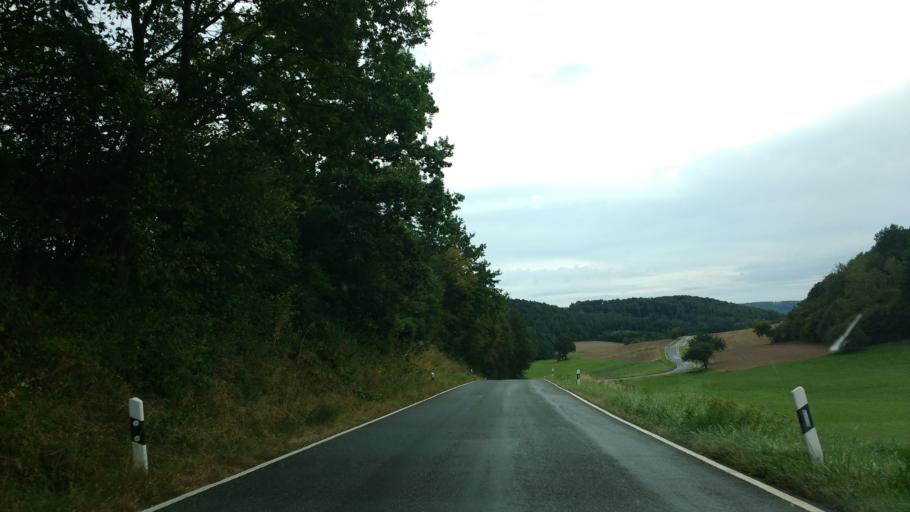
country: DE
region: Bavaria
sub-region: Regierungsbezirk Unterfranken
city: Geiselwind
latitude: 49.7978
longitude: 10.4932
